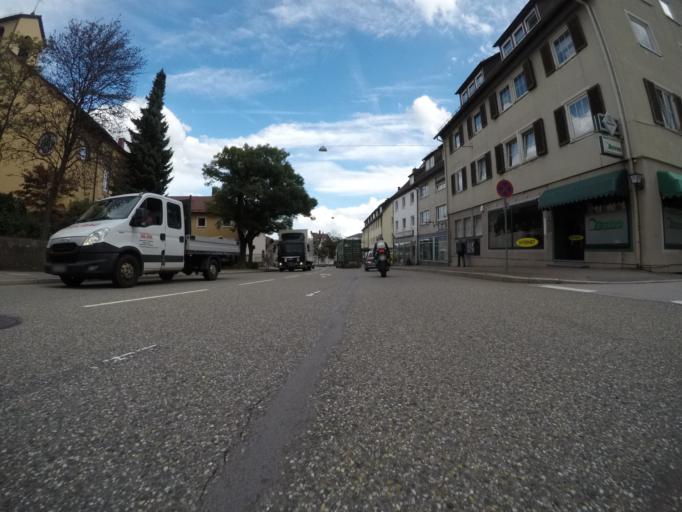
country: DE
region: Baden-Wuerttemberg
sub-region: Karlsruhe Region
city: Freudenstadt
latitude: 48.4645
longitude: 8.4148
